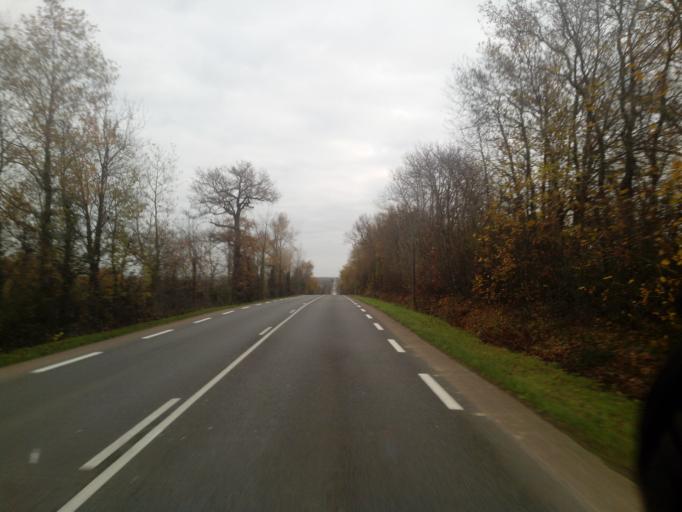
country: FR
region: Poitou-Charentes
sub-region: Departement des Deux-Sevres
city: Bressuire
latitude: 46.8307
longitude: -0.4307
